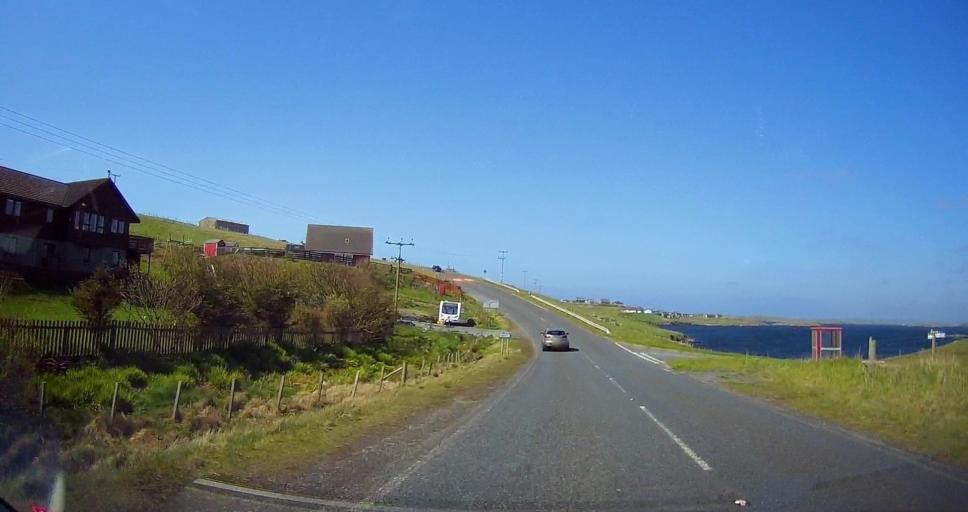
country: GB
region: Scotland
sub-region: Shetland Islands
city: Sandwick
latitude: 60.1046
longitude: -1.3188
